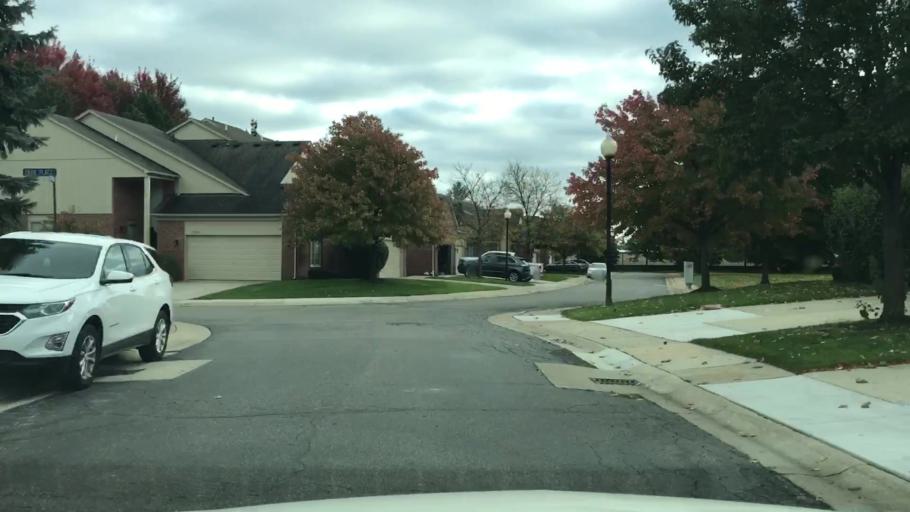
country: US
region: Michigan
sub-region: Macomb County
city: Shelby
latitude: 42.7003
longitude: -83.0706
